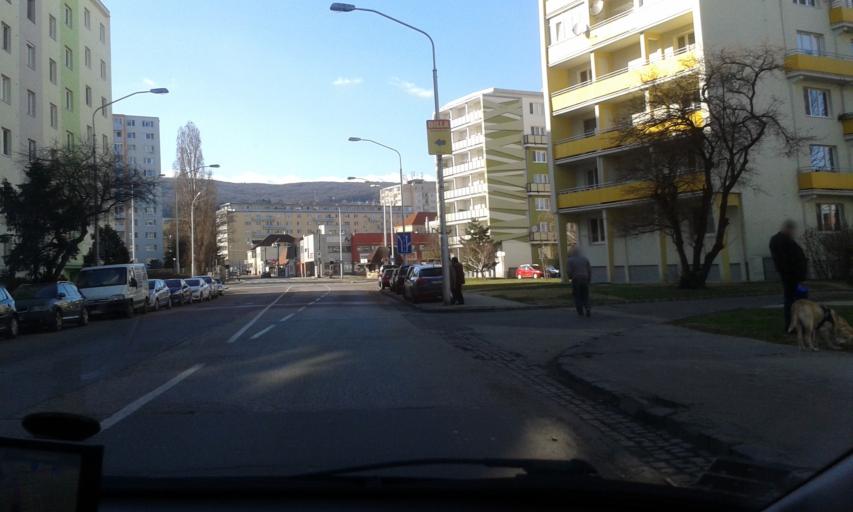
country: SK
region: Bratislavsky
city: Bratislava
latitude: 48.1729
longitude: 17.1309
